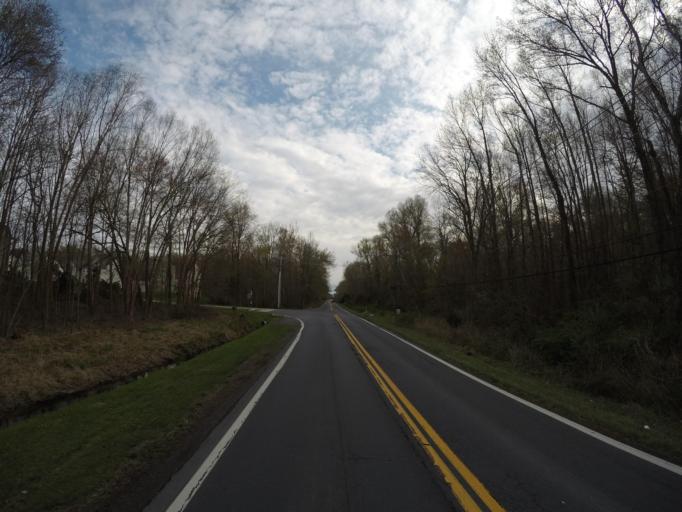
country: US
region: Delaware
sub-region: New Castle County
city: Glasgow
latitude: 39.5745
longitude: -75.7642
